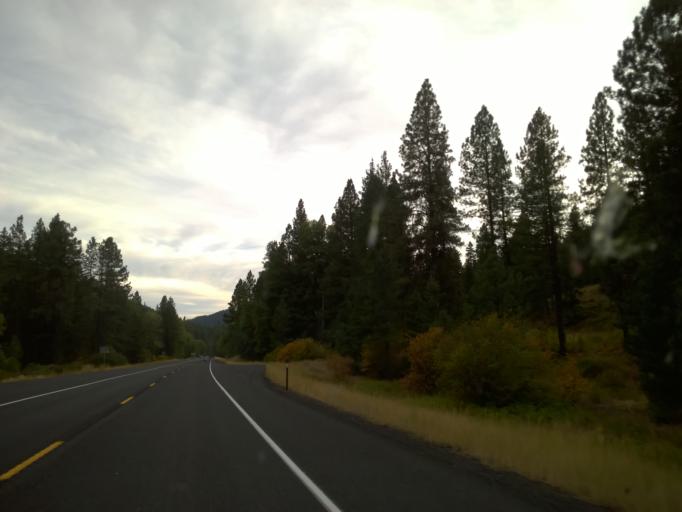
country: US
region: Washington
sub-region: Kittitas County
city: Cle Elum
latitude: 47.3099
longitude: -120.6939
